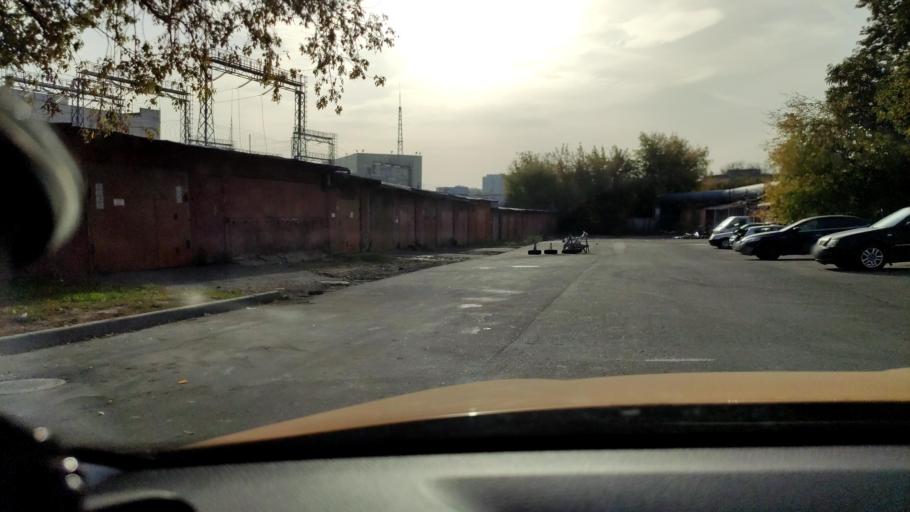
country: RU
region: Moscow
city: Novyye Cheremushki
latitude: 55.6988
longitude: 37.5835
